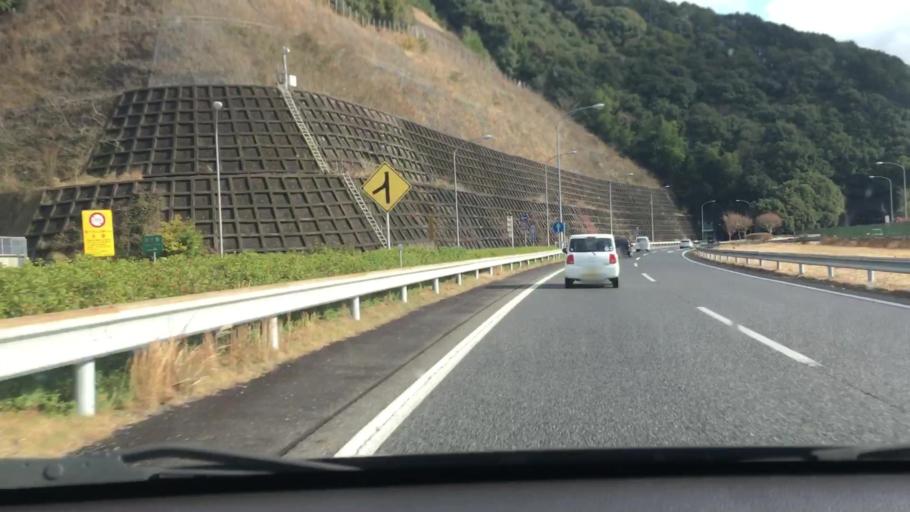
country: JP
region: Kumamoto
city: Yatsushiro
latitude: 32.4422
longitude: 130.6693
